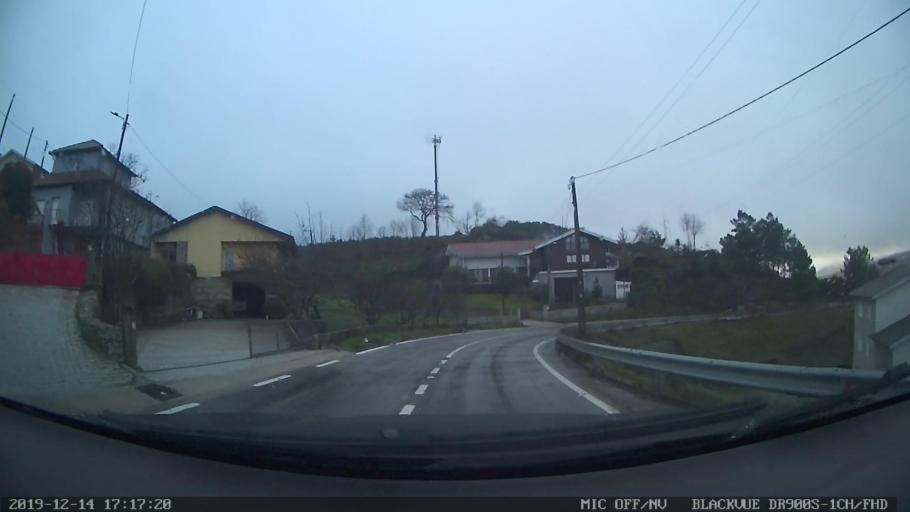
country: PT
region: Vila Real
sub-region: Vila Pouca de Aguiar
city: Vila Pouca de Aguiar
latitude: 41.4990
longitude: -7.6368
